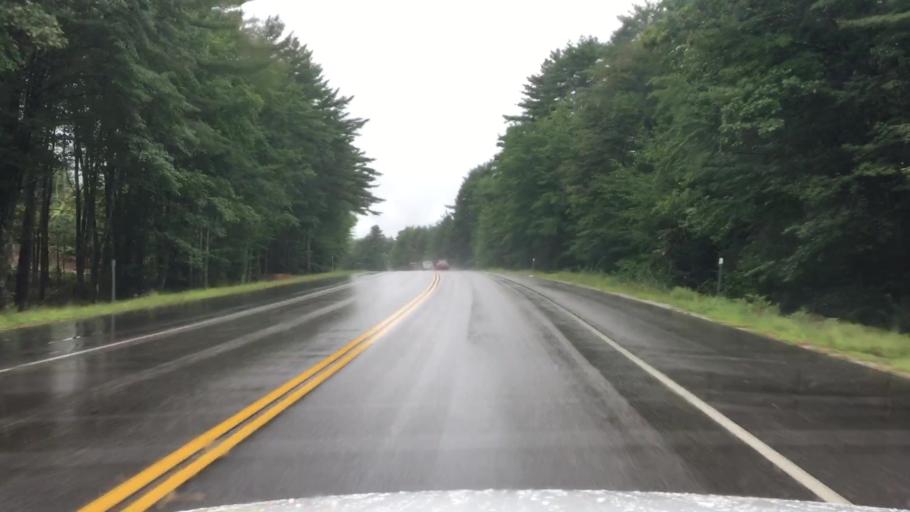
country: US
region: New Hampshire
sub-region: Carroll County
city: Conway
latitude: 43.9970
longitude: -71.0729
